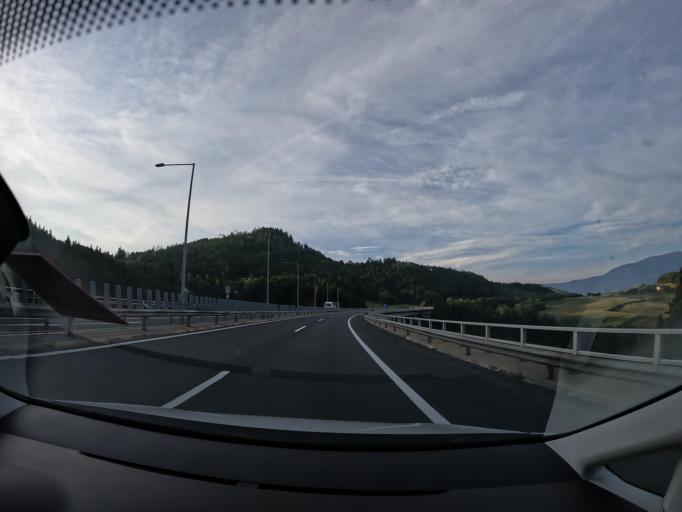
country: AT
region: Carinthia
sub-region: Politischer Bezirk Volkermarkt
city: Griffen
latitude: 46.7082
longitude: 14.7774
